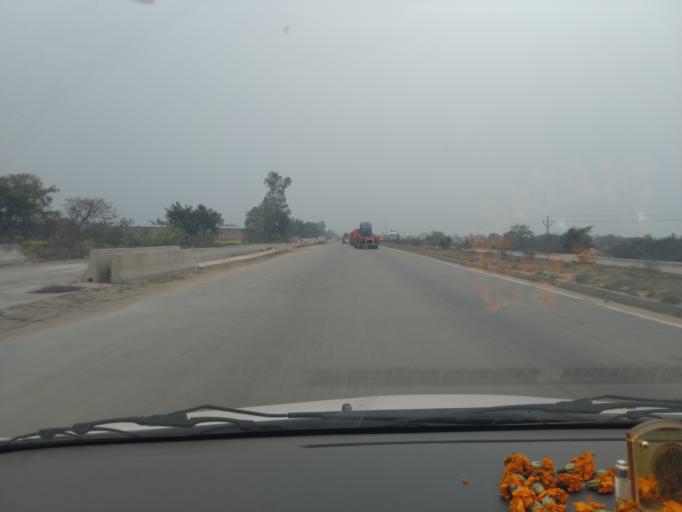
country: IN
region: Bihar
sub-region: Rohtas
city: Dehri
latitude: 24.9698
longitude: 83.9189
